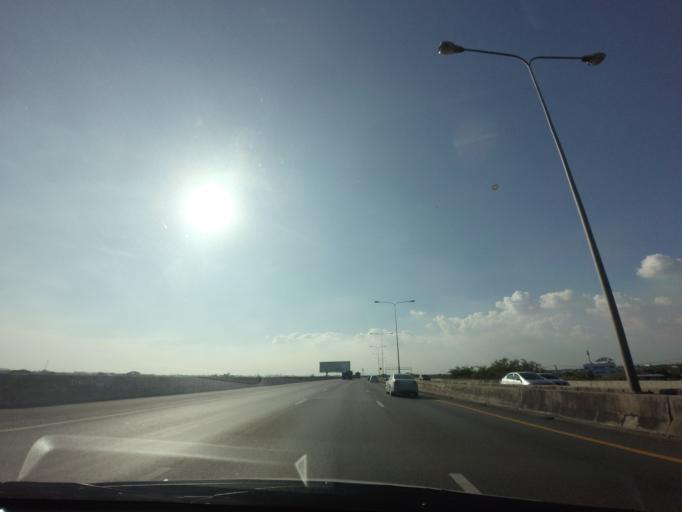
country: TH
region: Samut Prakan
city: Samut Prakan
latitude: 13.6001
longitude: 100.6454
